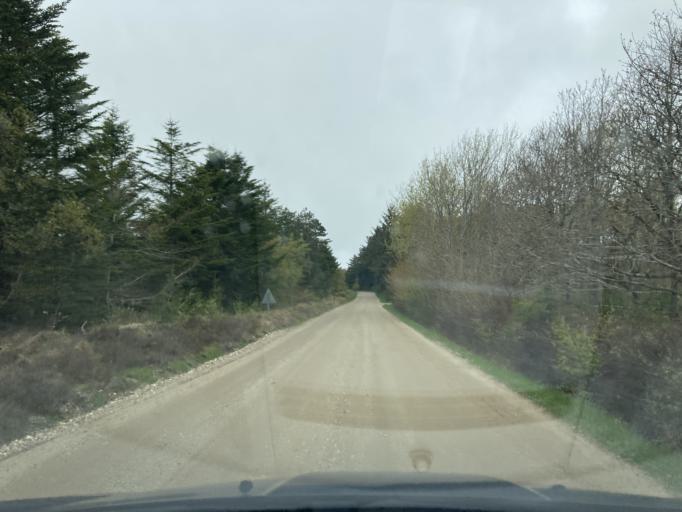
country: DK
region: Central Jutland
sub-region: Lemvig Kommune
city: Thyboron
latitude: 56.8207
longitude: 8.2676
